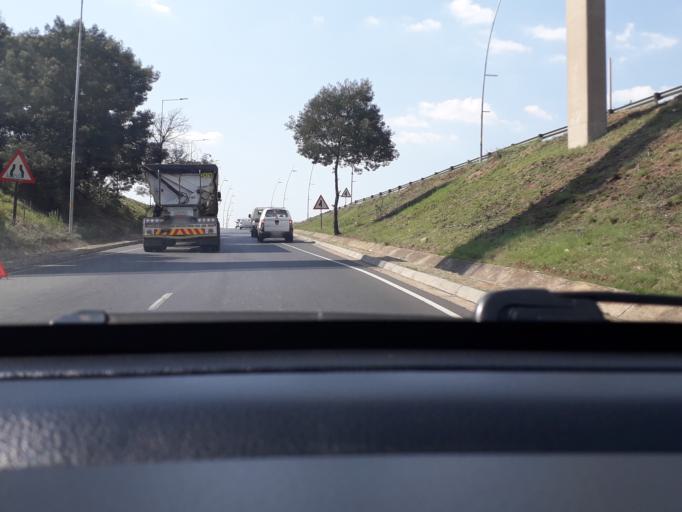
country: ZA
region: Gauteng
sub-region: City of Johannesburg Metropolitan Municipality
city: Modderfontein
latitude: -26.0886
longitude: 28.1904
